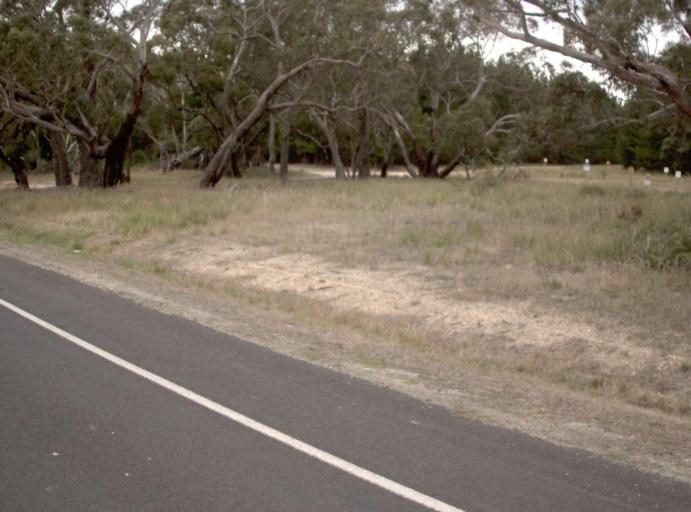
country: AU
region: Victoria
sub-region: Wellington
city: Sale
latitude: -38.2200
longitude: 147.0588
